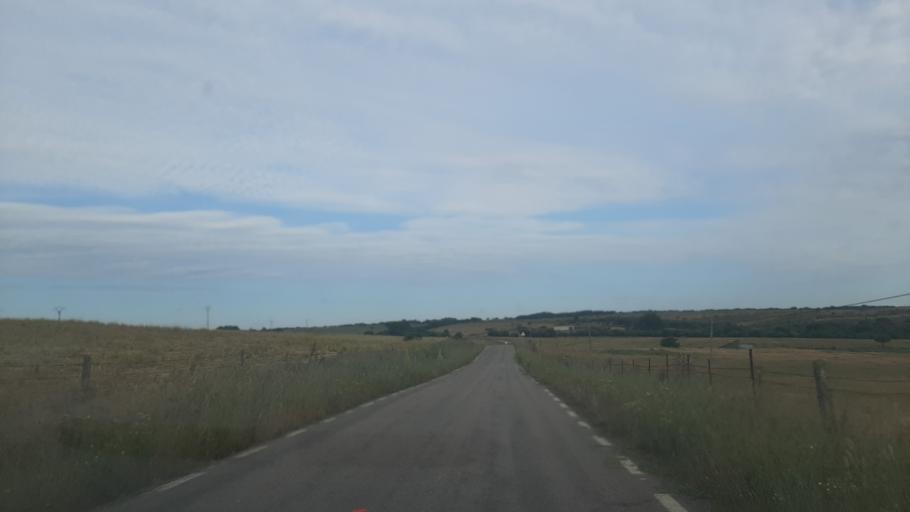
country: ES
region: Castille and Leon
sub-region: Provincia de Salamanca
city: Gallegos de Arganan
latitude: 40.6350
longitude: -6.7141
